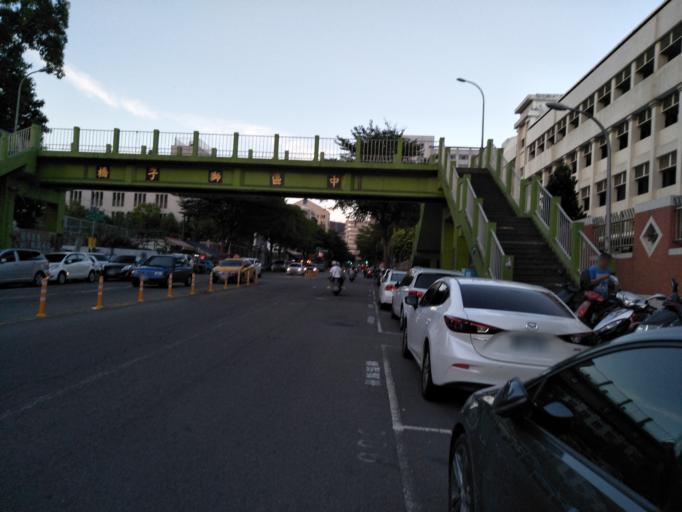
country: TW
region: Taiwan
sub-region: Taichung City
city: Taichung
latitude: 24.1495
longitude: 120.6811
